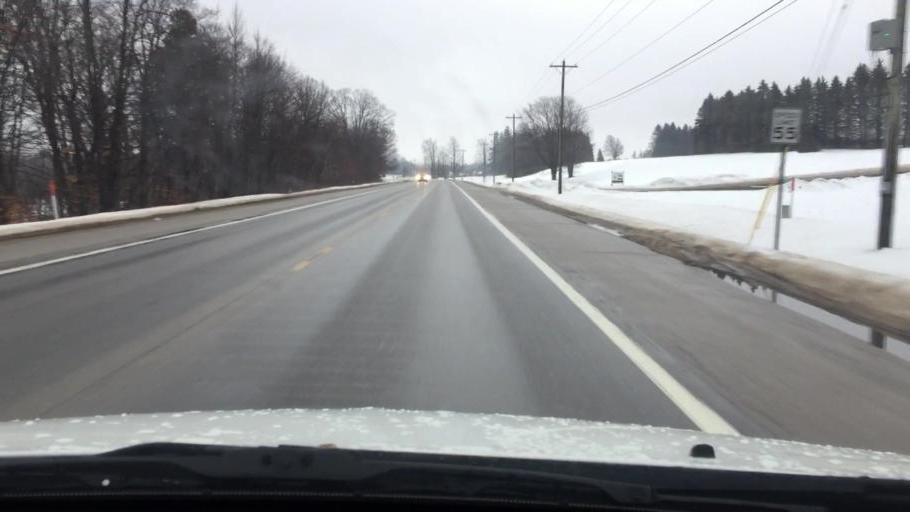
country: US
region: Michigan
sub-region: Charlevoix County
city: Charlevoix
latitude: 45.2860
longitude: -85.2427
